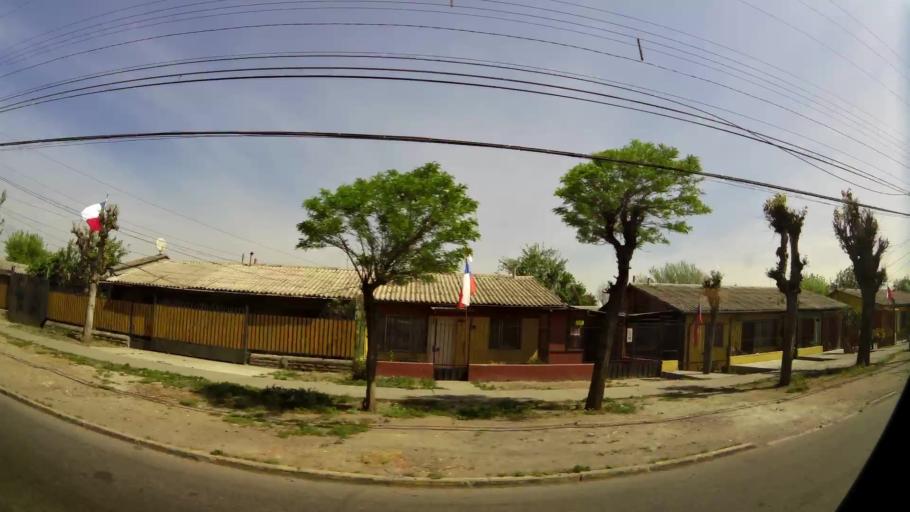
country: CL
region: Santiago Metropolitan
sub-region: Provincia de Santiago
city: Lo Prado
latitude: -33.4105
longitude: -70.7070
